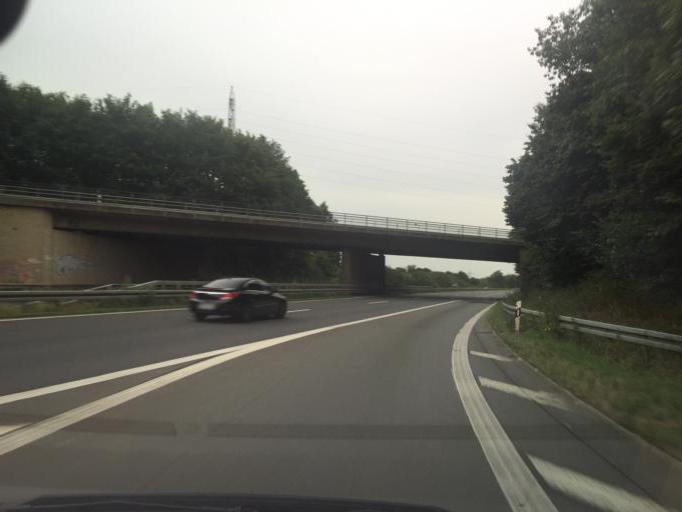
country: DE
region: North Rhine-Westphalia
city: Erkelenz
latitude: 51.0807
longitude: 6.3372
